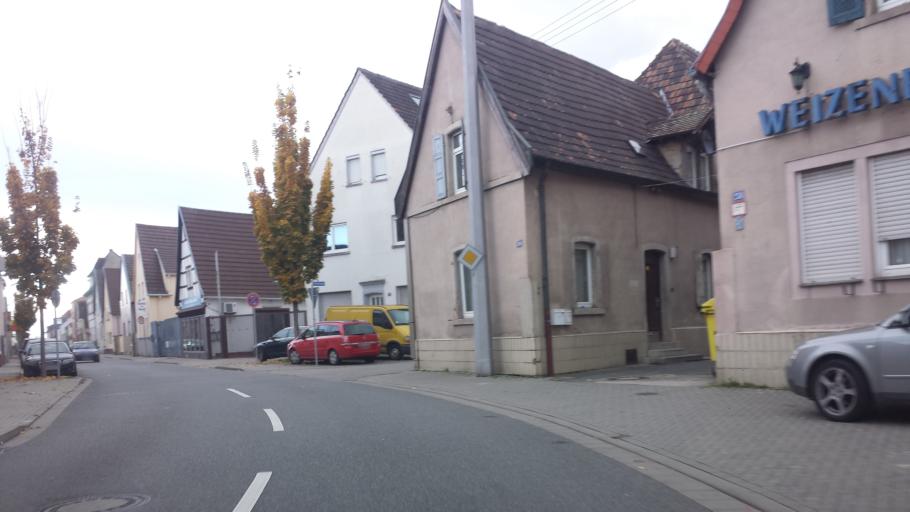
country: DE
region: Rheinland-Pfalz
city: Neuhofen
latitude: 49.4455
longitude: 8.4216
